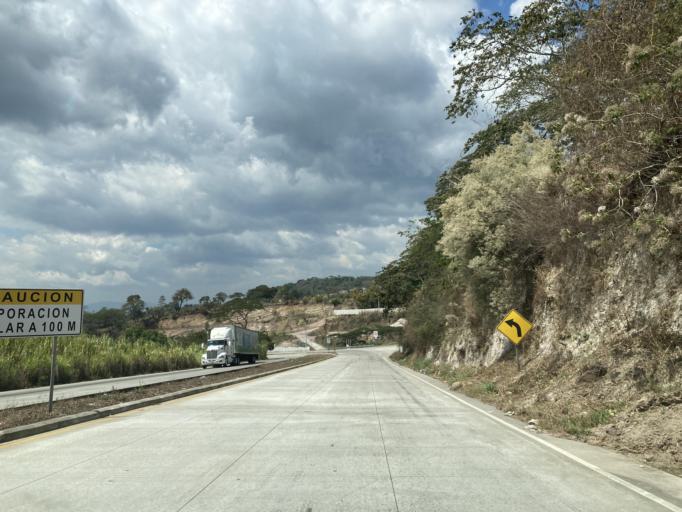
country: GT
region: Santa Rosa
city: Barberena
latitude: 14.3010
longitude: -90.3660
